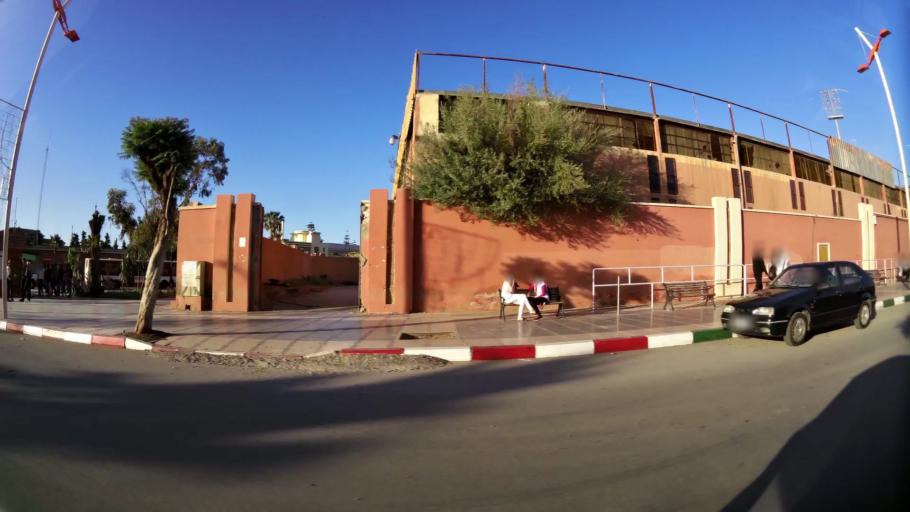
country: MA
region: Oriental
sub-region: Berkane-Taourirt
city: Berkane
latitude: 34.9276
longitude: -2.3279
